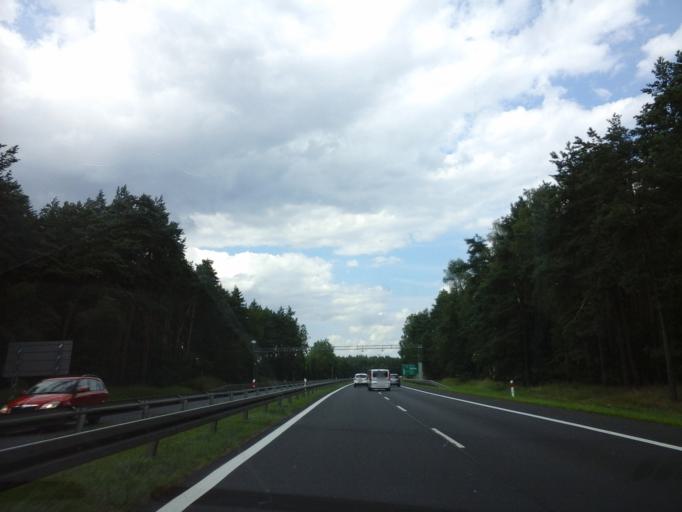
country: PL
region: West Pomeranian Voivodeship
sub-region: Powiat goleniowski
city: Goleniow
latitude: 53.5613
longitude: 14.7958
